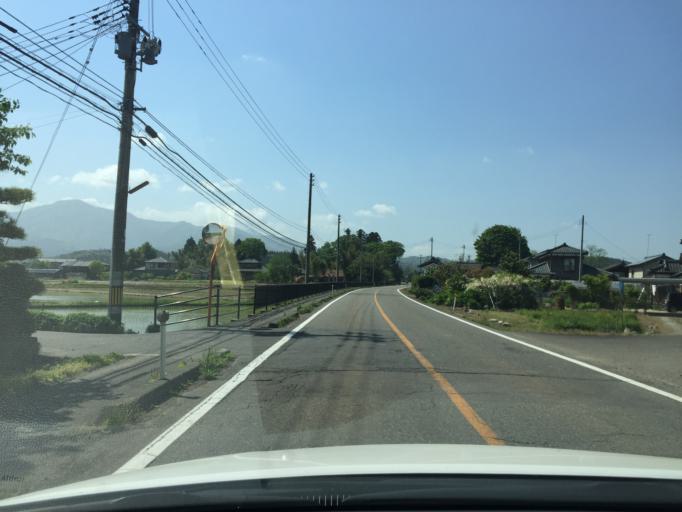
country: JP
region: Niigata
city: Muramatsu
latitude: 37.6789
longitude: 139.1497
